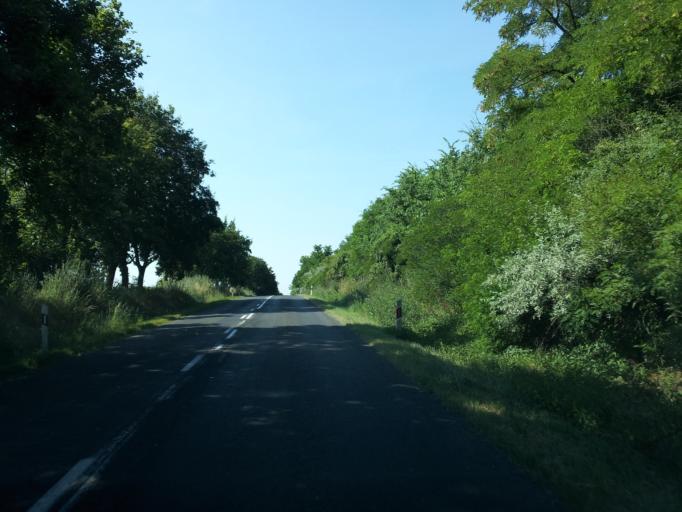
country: HU
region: Fejer
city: Lovasbereny
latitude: 47.3486
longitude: 18.5794
